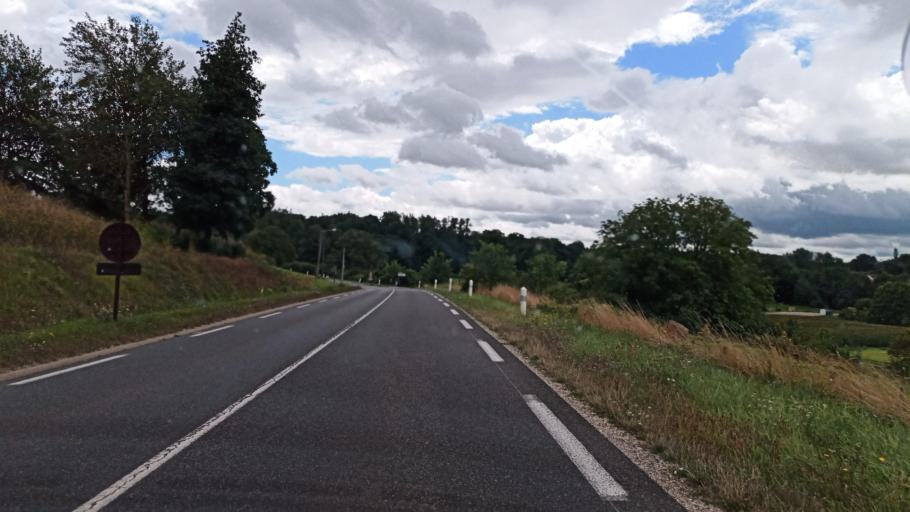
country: FR
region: Ile-de-France
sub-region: Departement de Seine-et-Marne
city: Voulx
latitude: 48.2947
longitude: 2.9479
